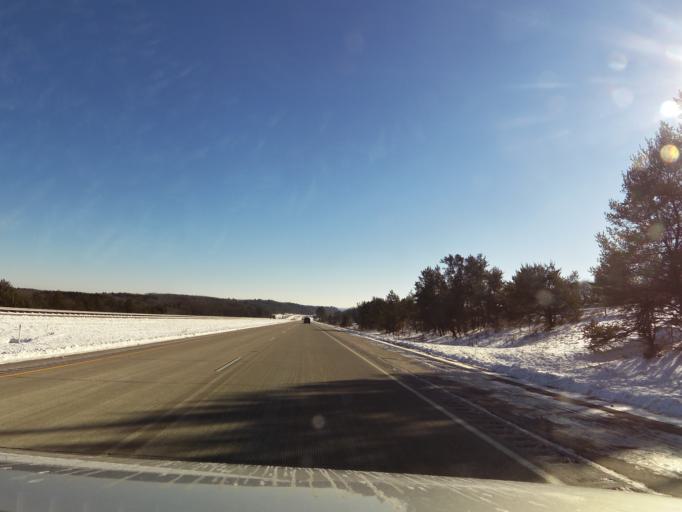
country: US
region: Wisconsin
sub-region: Jackson County
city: Black River Falls
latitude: 44.3376
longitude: -90.9079
